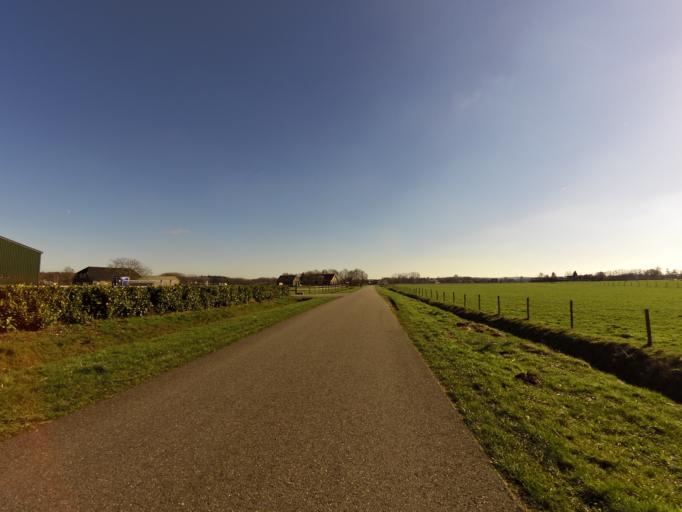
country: NL
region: Gelderland
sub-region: Gemeente Doesburg
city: Doesburg
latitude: 51.9528
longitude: 6.1619
